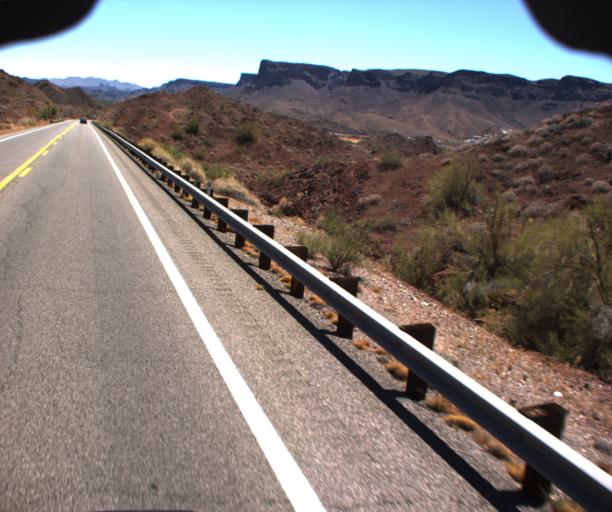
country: US
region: Arizona
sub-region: La Paz County
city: Cienega Springs
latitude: 34.3106
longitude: -114.1037
